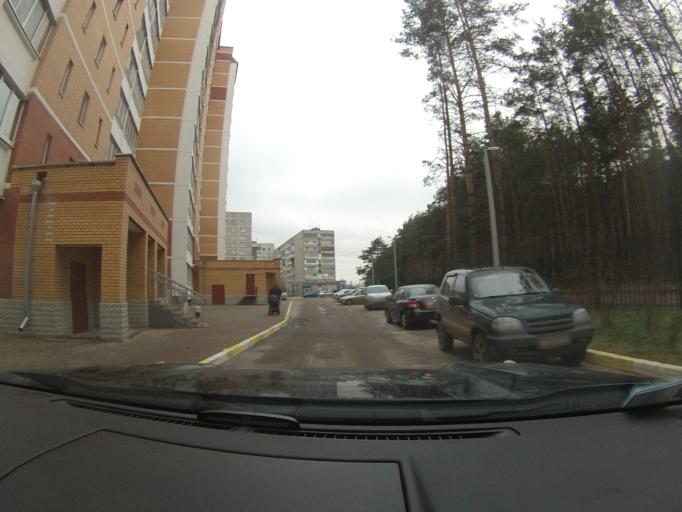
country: RU
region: Moskovskaya
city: Peski
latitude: 55.2765
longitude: 38.7570
